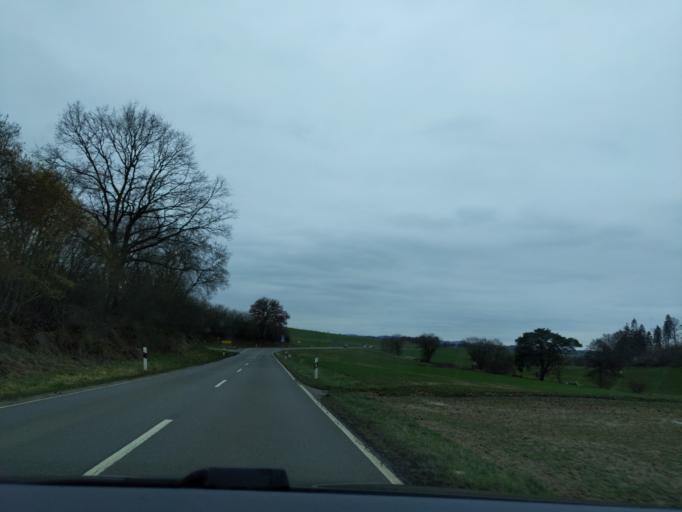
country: DE
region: Hesse
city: Frankenberg
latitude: 51.0356
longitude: 8.8203
